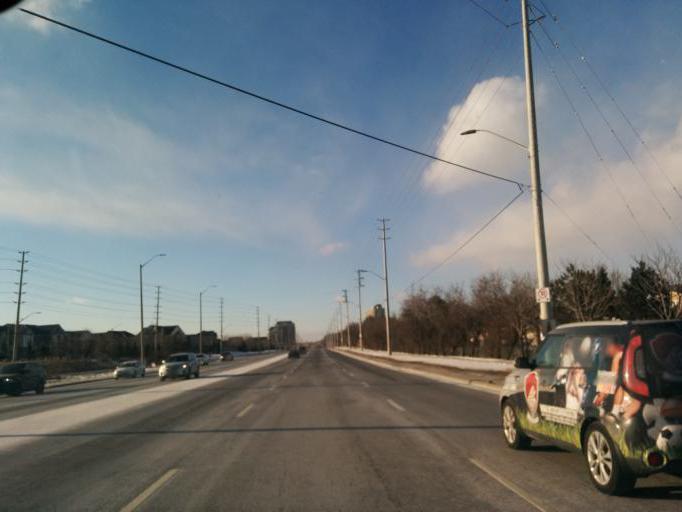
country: CA
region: Ontario
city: Mississauga
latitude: 43.5873
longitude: -79.6622
